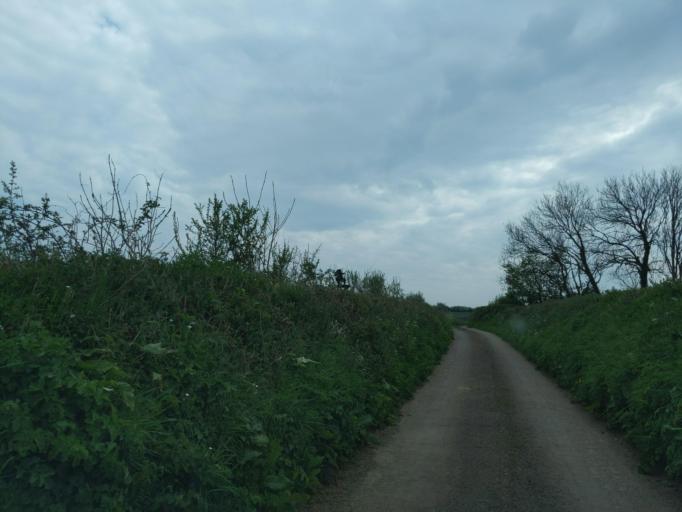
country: GB
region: England
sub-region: Devon
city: Yealmpton
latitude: 50.3651
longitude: -4.0245
